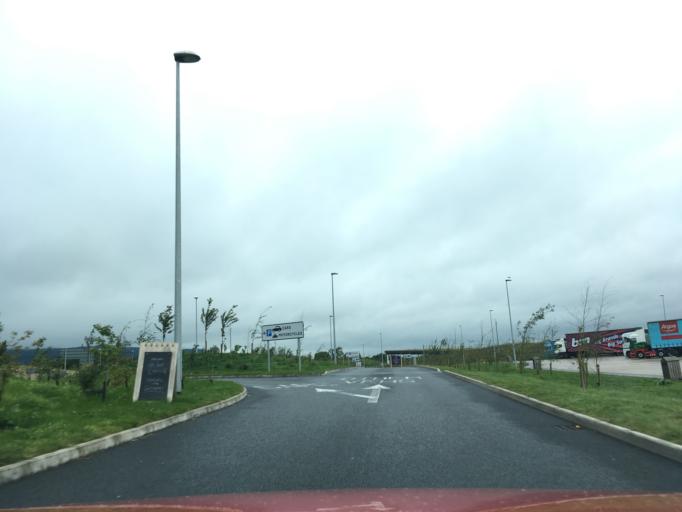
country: GB
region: England
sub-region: Gloucestershire
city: Painswick
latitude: 51.8195
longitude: -2.2238
